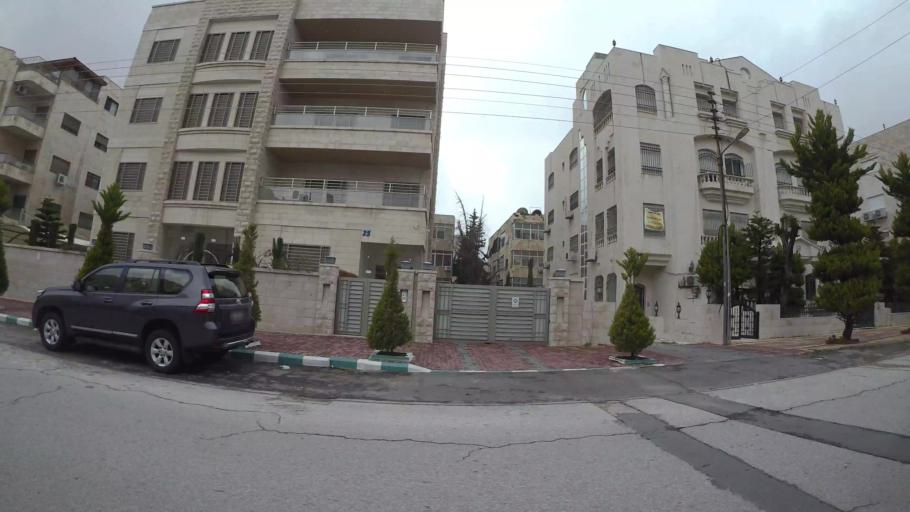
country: JO
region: Amman
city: Wadi as Sir
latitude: 31.9528
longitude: 35.8607
